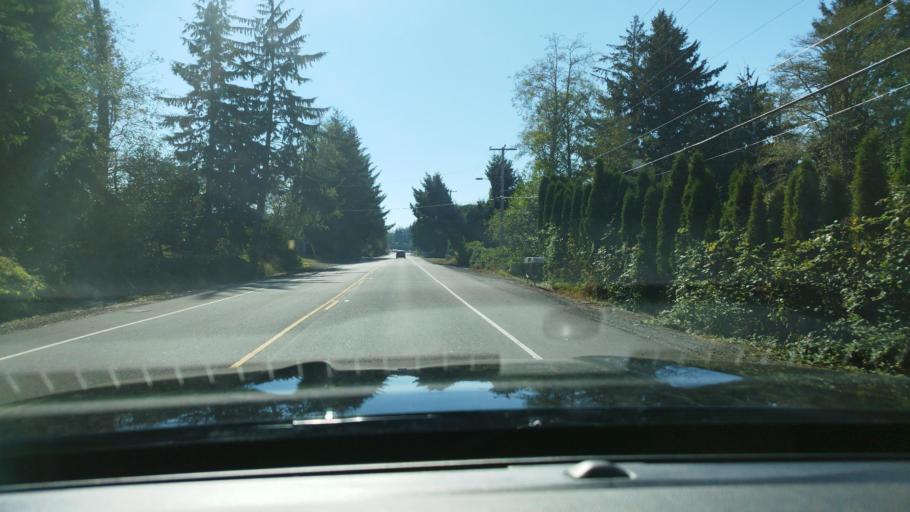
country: US
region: Oregon
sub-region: Clatsop County
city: Warrenton
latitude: 46.1529
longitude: -123.9159
